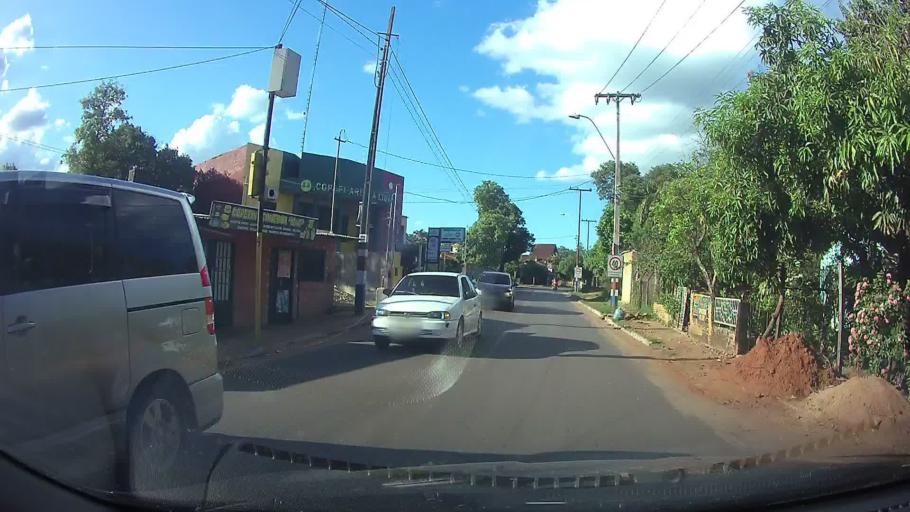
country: PY
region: Central
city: Aregua
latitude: -25.2927
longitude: -57.4414
